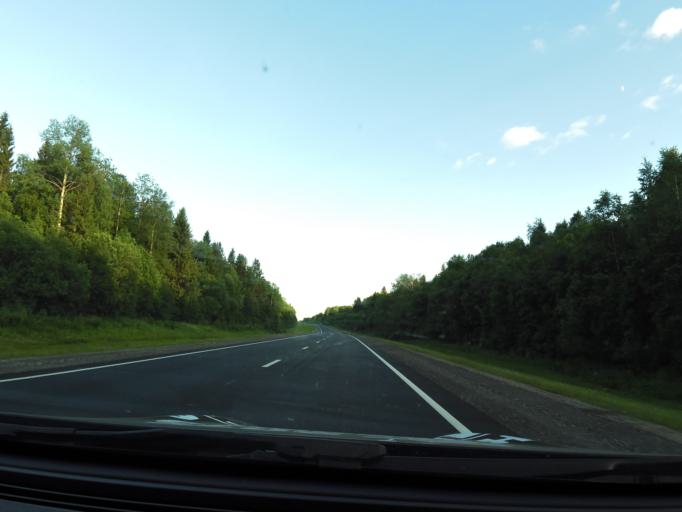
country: RU
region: Vologda
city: Gryazovets
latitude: 58.9162
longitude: 40.1772
